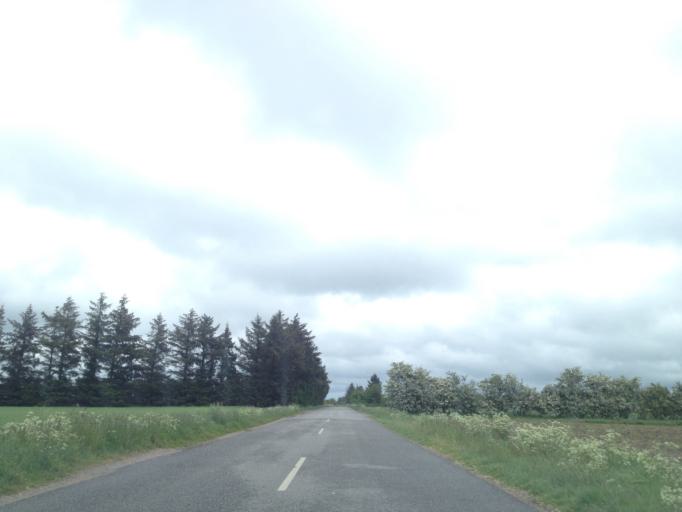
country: DK
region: South Denmark
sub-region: Tonder Kommune
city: Sherrebek
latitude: 55.0789
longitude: 8.7815
